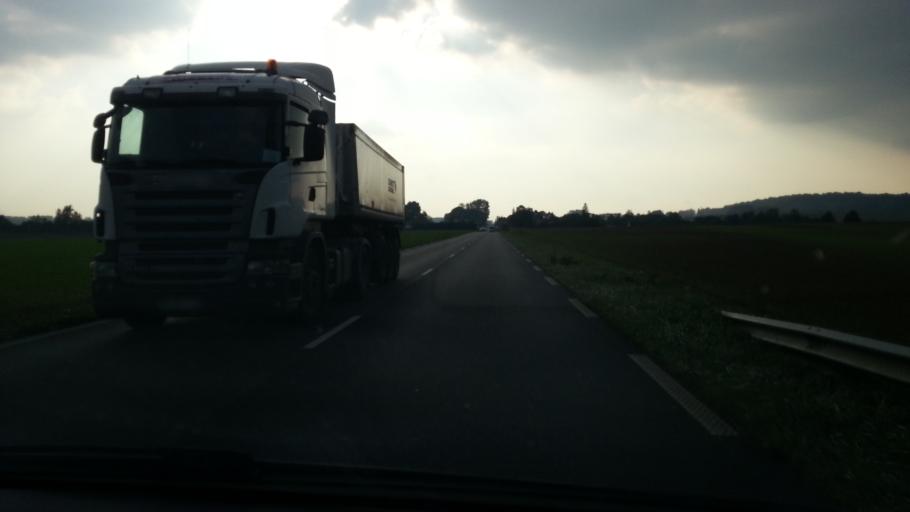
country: FR
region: Picardie
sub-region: Departement de l'Aisne
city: Ognes
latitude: 49.5946
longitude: 3.1200
